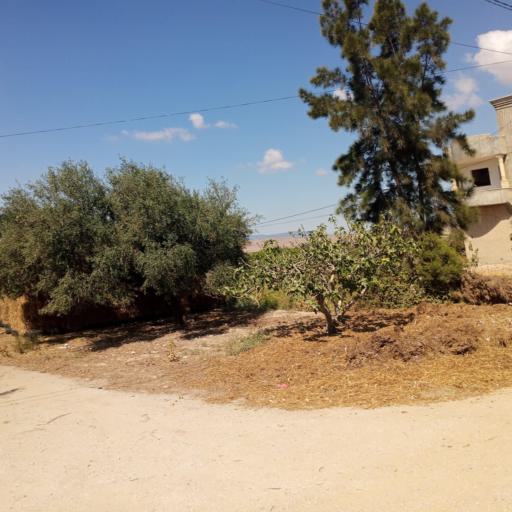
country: TN
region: Nabul
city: Qulaybiyah
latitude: 36.8561
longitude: 11.0356
